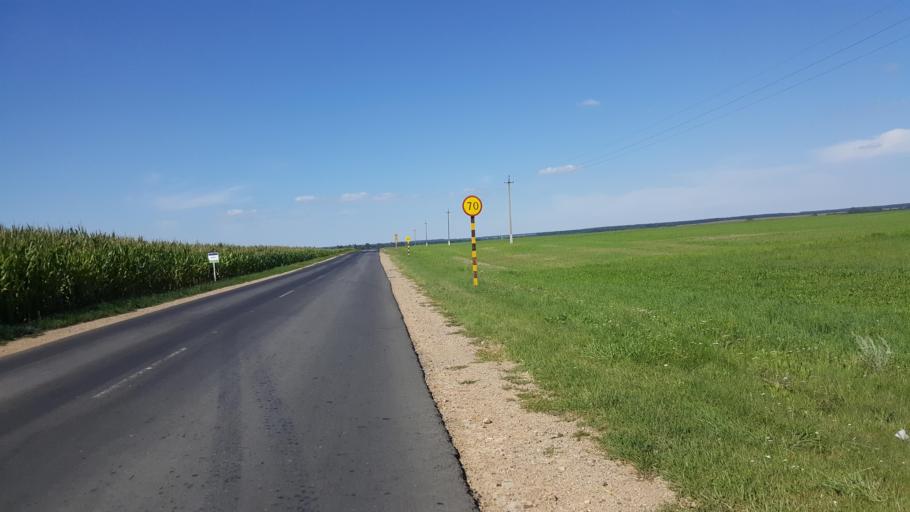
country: BY
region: Brest
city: Charnawchytsy
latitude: 52.2863
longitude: 23.6043
